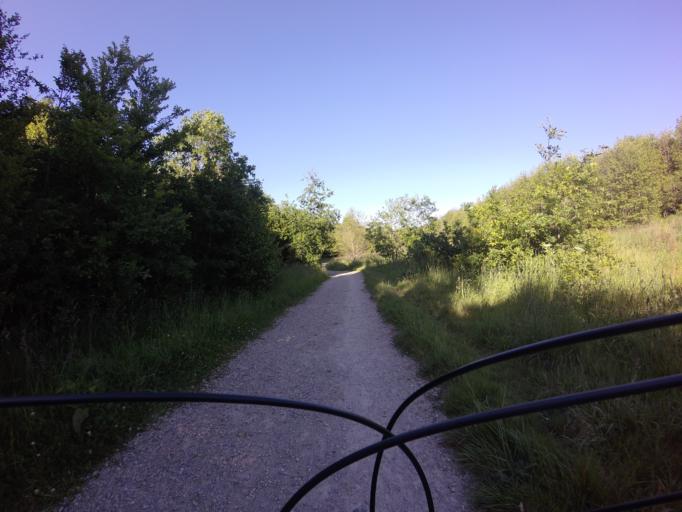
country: FR
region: Brittany
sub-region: Departement du Finistere
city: Quimper
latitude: 48.0153
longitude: -4.1200
